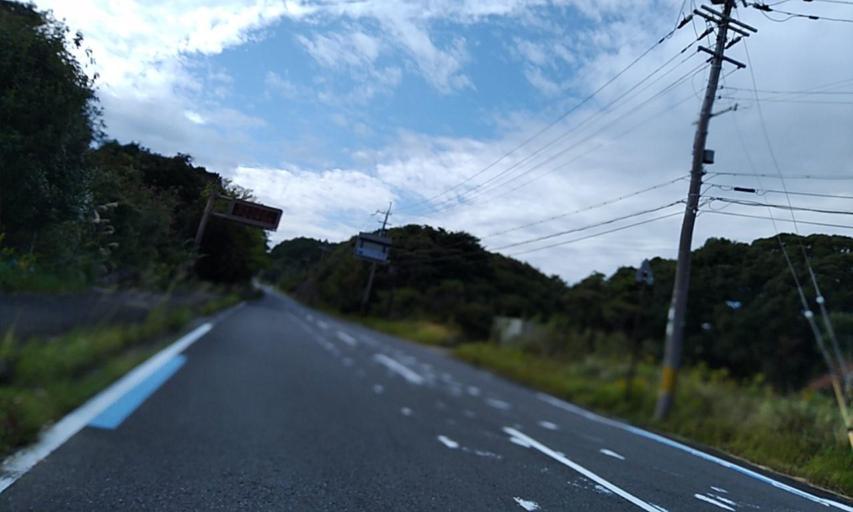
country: JP
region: Wakayama
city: Shingu
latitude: 33.4723
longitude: 135.8172
